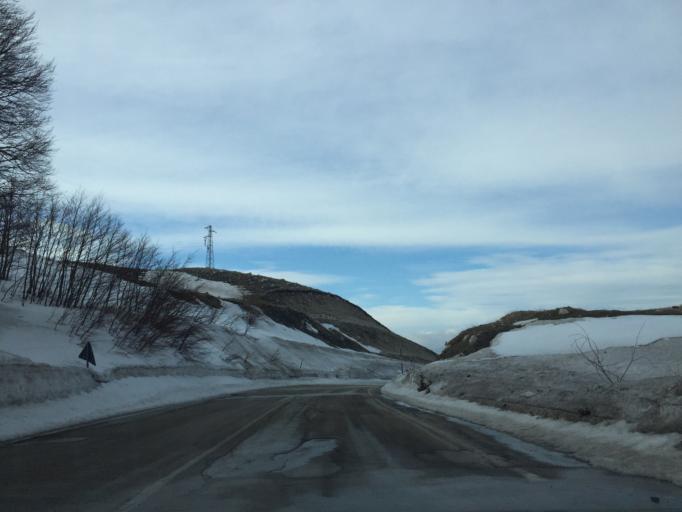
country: IT
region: Molise
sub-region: Provincia di Campobasso
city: San Massimo
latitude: 41.4648
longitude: 14.3945
